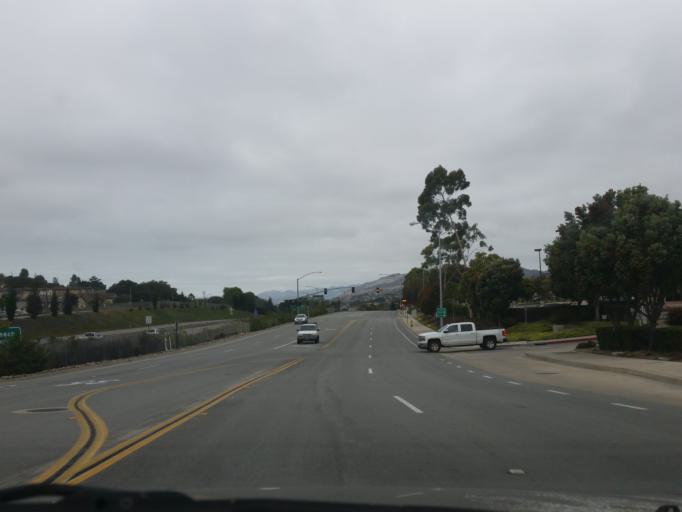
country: US
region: California
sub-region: San Luis Obispo County
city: Arroyo Grande
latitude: 35.1261
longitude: -120.5961
